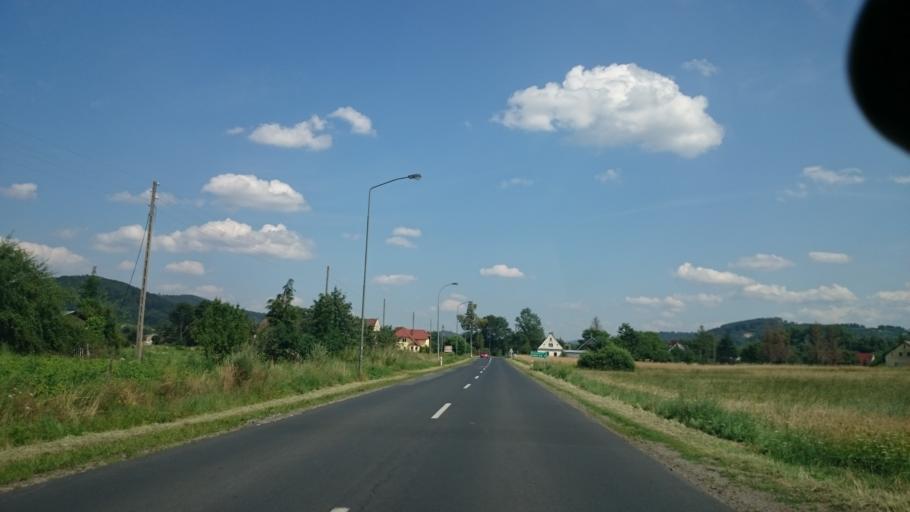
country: PL
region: Lower Silesian Voivodeship
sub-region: Powiat klodzki
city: Klodzko
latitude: 50.3684
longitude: 16.6826
